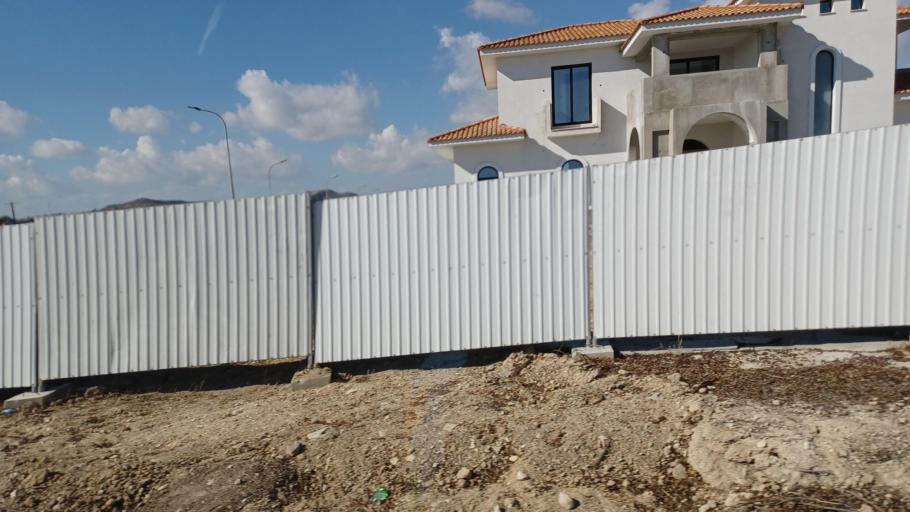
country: CY
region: Larnaka
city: Pyla
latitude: 34.9939
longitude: 33.6835
